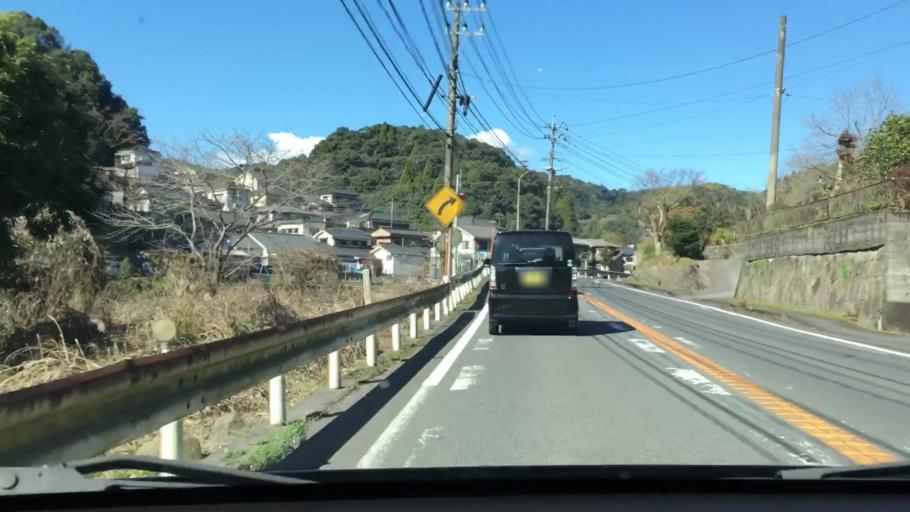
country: JP
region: Kagoshima
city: Kagoshima-shi
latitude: 31.6494
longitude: 130.5131
